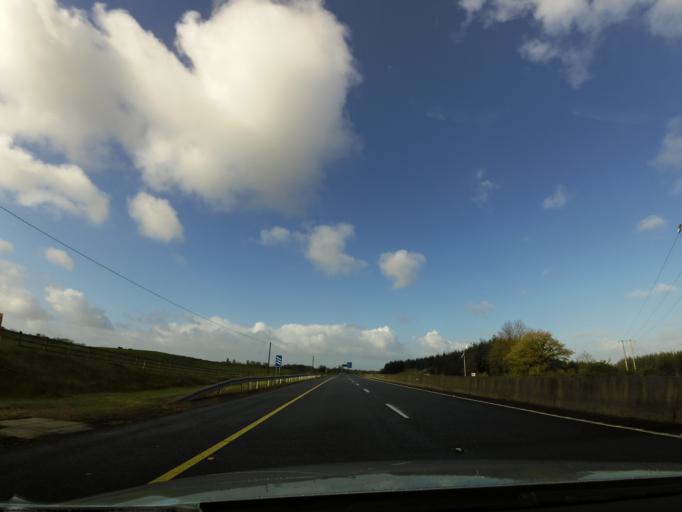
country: IE
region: Munster
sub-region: North Tipperary
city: Newport
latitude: 52.7623
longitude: -8.3967
